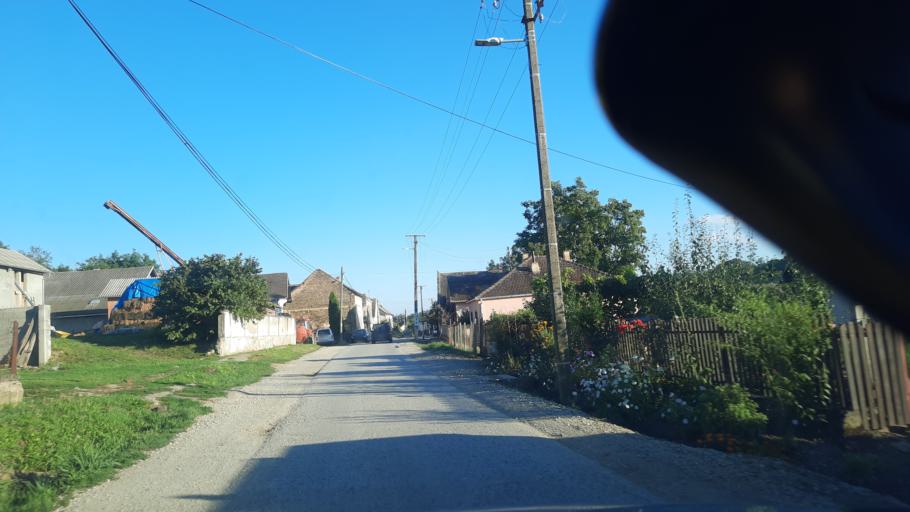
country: RS
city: Cortanovci
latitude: 45.1168
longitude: 19.9456
